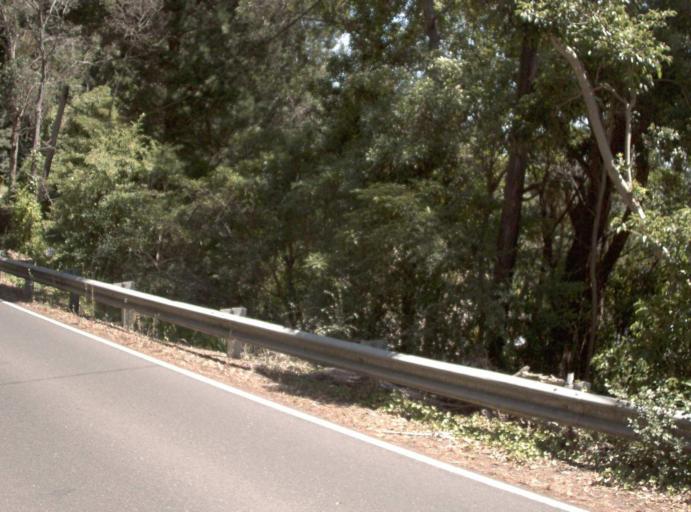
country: AU
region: Victoria
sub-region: Yarra Ranges
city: Kalorama
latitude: -37.8120
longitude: 145.3646
